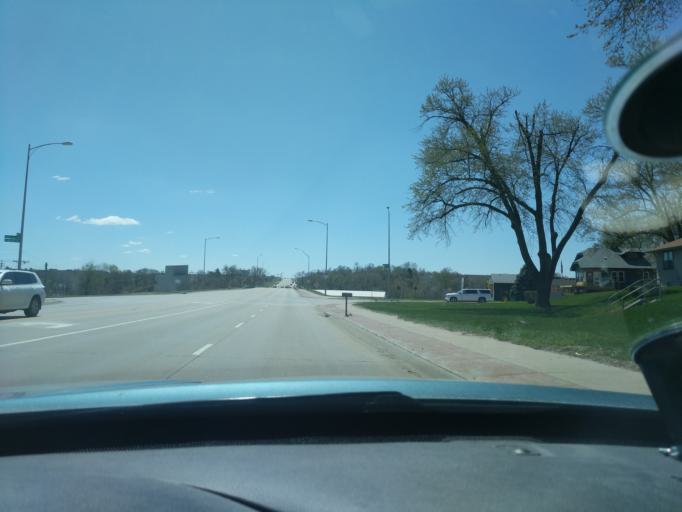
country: US
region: Nebraska
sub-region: Douglas County
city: Elkhorn
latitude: 41.2837
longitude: -96.2346
